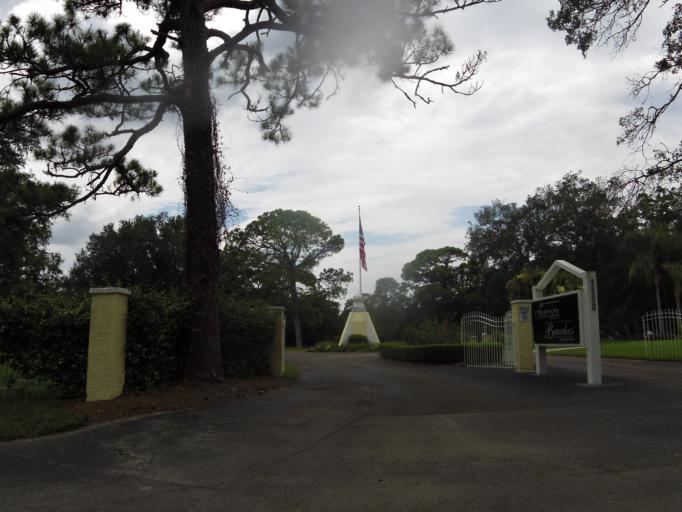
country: US
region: Florida
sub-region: Duval County
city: Atlantic Beach
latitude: 30.3364
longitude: -81.4218
